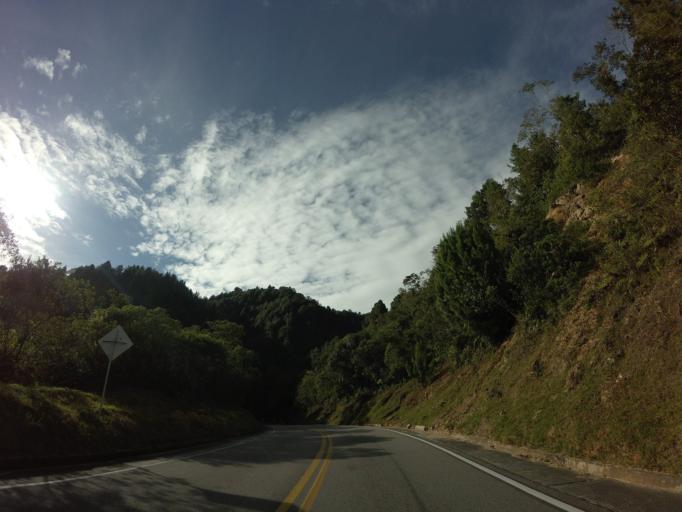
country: CO
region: Tolima
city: Herveo
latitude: 5.1371
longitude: -75.1671
